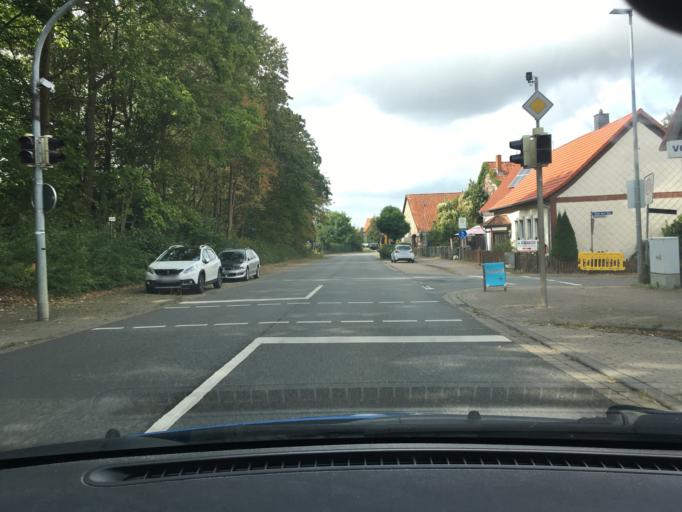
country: DE
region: Lower Saxony
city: Messenkamp
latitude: 52.2335
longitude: 9.4164
